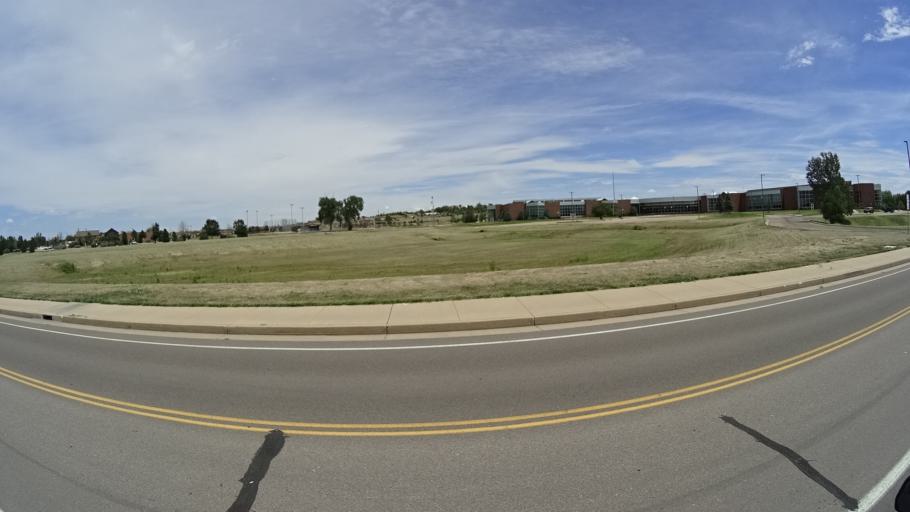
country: US
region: Colorado
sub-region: El Paso County
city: Fountain
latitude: 38.6732
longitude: -104.6864
